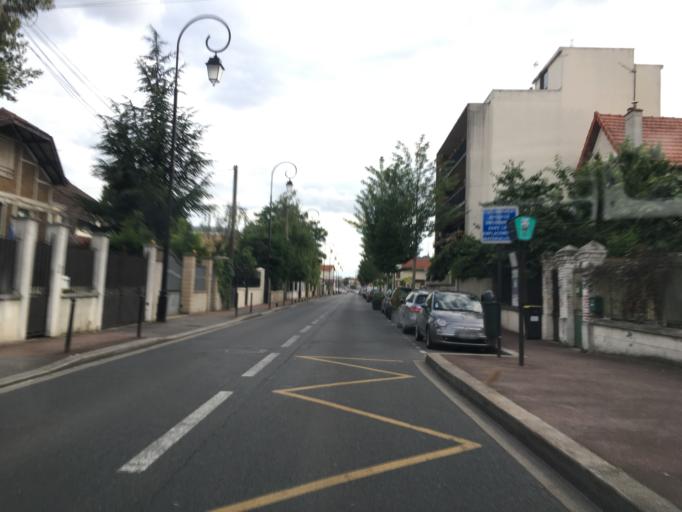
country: FR
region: Ile-de-France
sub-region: Departement du Val-de-Marne
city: Saint-Maur-des-Fosses
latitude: 48.7955
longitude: 2.4993
